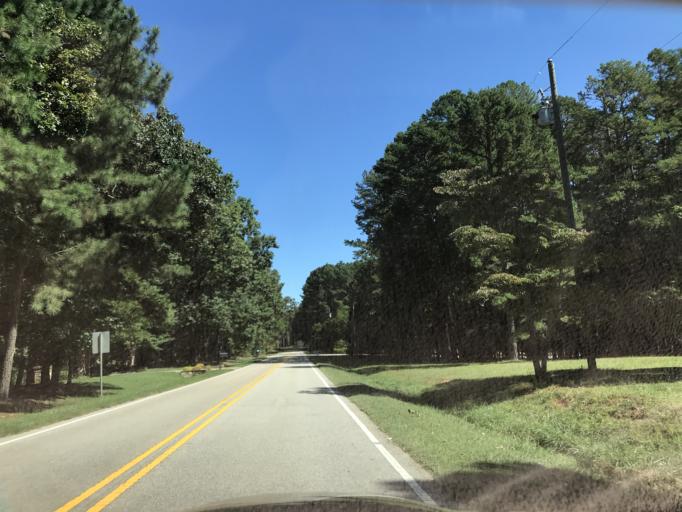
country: US
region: North Carolina
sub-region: Wake County
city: Wake Forest
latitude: 35.9571
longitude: -78.6205
